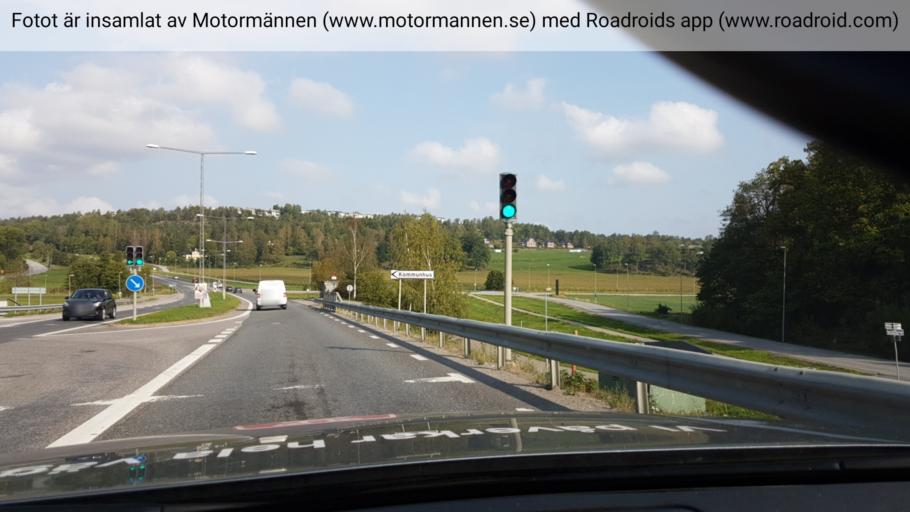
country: SE
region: Stockholm
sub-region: Botkyrka Kommun
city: Tumba
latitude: 59.2009
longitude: 17.8416
